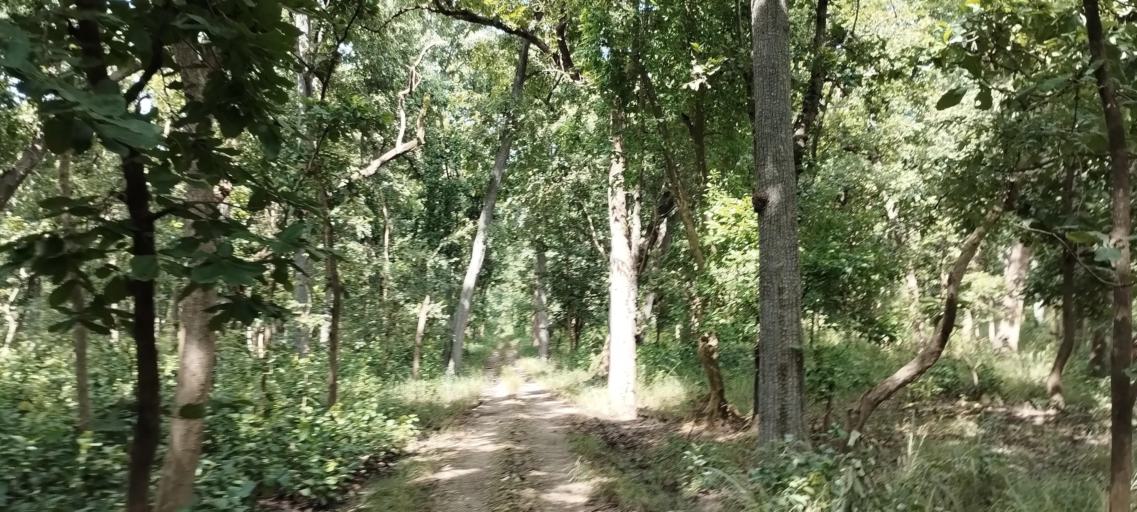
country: NP
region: Far Western
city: Tikapur
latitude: 28.5237
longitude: 81.2790
